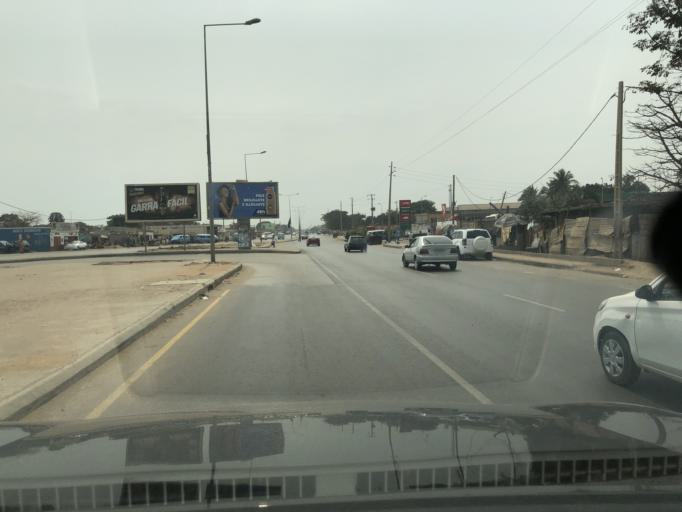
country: AO
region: Luanda
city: Luanda
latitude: -8.7991
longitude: 13.3148
